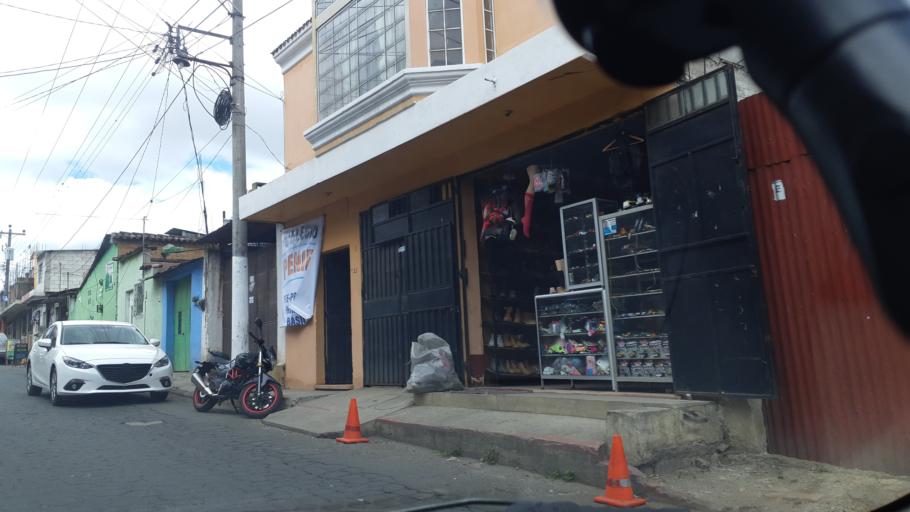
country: GT
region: Chimaltenango
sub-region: Municipio de Chimaltenango
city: Chimaltenango
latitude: 14.6629
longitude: -90.8214
